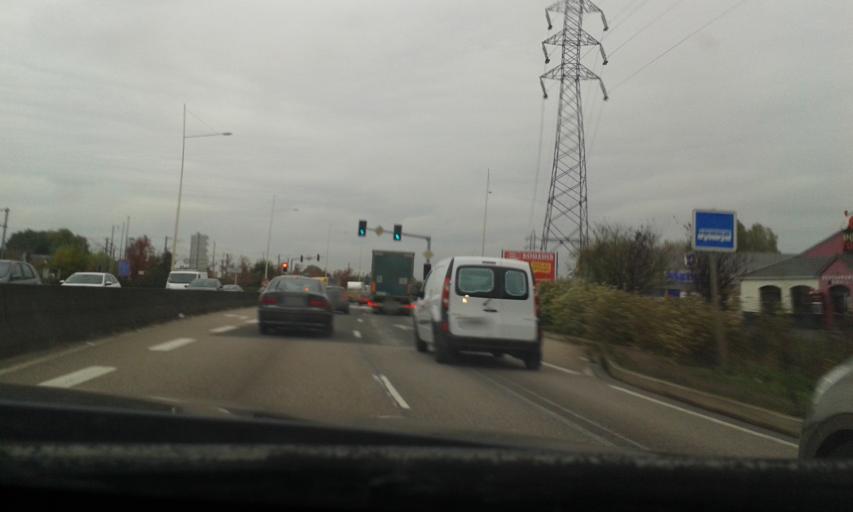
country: FR
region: Haute-Normandie
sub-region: Departement de la Seine-Maritime
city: Saint-Etienne-du-Rouvray
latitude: 49.3801
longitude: 1.1105
